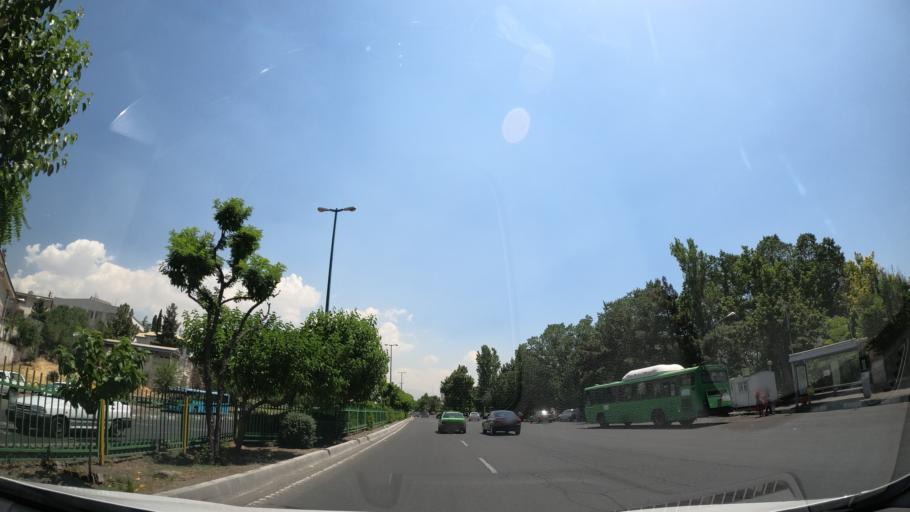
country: IR
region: Tehran
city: Tajrish
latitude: 35.7555
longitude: 51.3707
